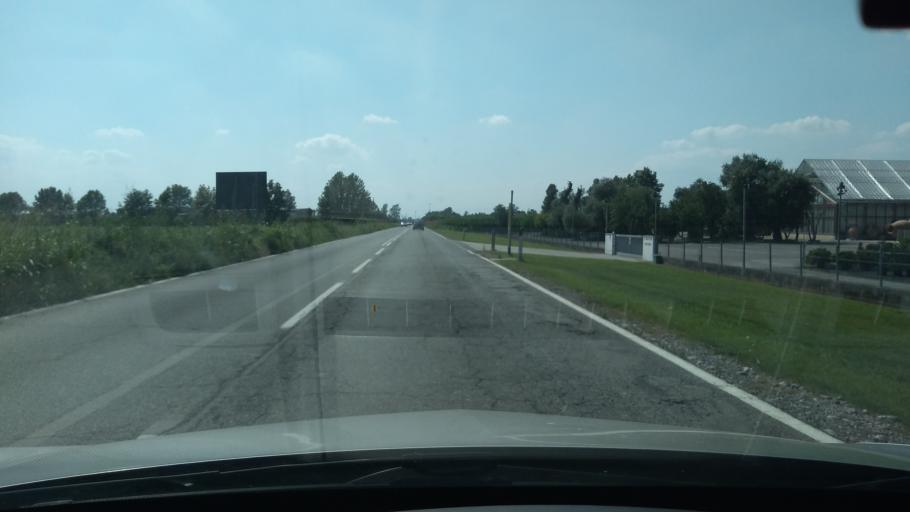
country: IT
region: Lombardy
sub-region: Provincia di Bergamo
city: Mornico al Serio
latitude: 45.5949
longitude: 9.7845
